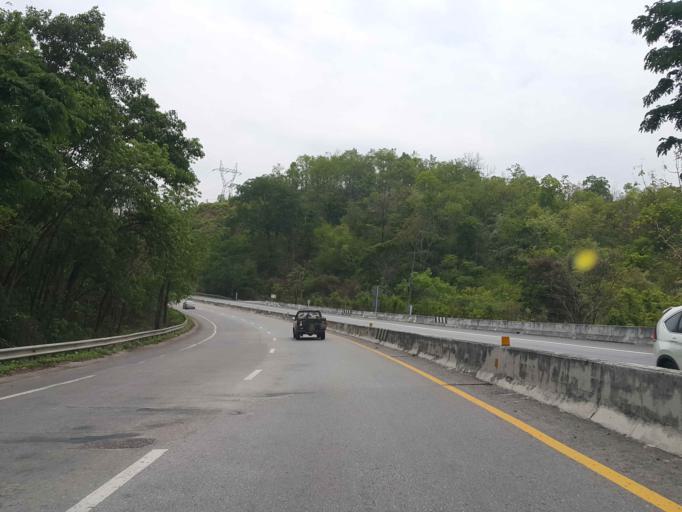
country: TH
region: Lampang
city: Sop Prap
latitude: 17.8276
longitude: 99.2839
